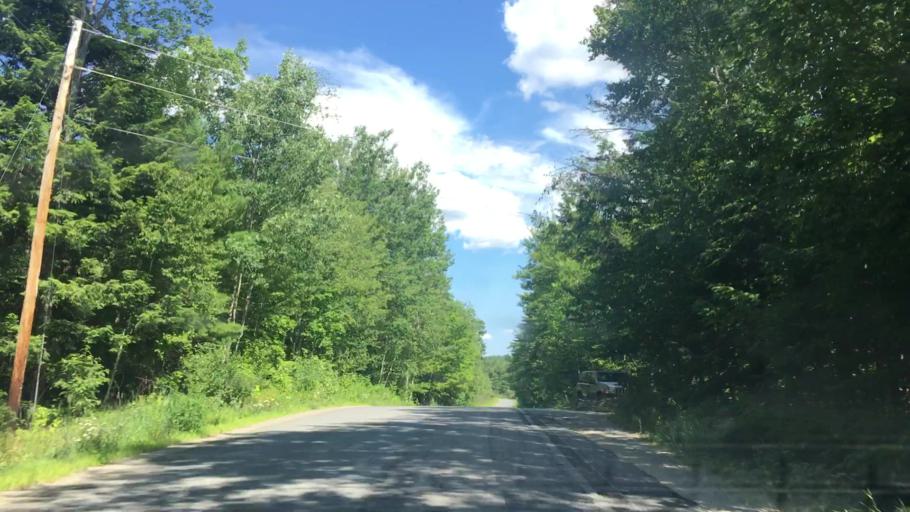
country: US
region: Maine
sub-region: Franklin County
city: Chesterville
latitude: 44.5536
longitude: -70.1023
